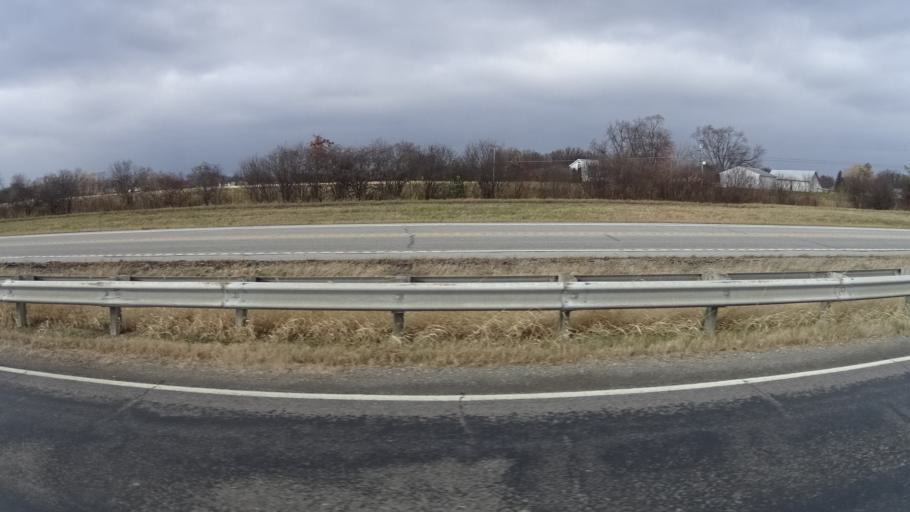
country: US
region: Ohio
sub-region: Lorain County
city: Oberlin
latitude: 41.2784
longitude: -82.1885
